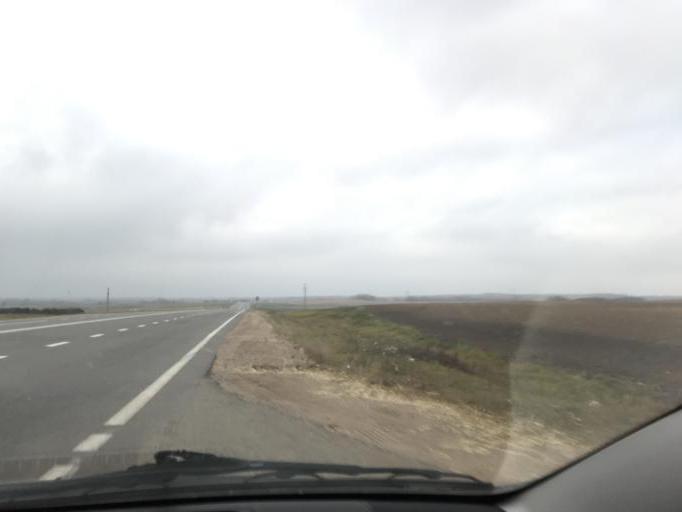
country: BY
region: Vitebsk
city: Vitebsk
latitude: 55.1495
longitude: 30.0666
